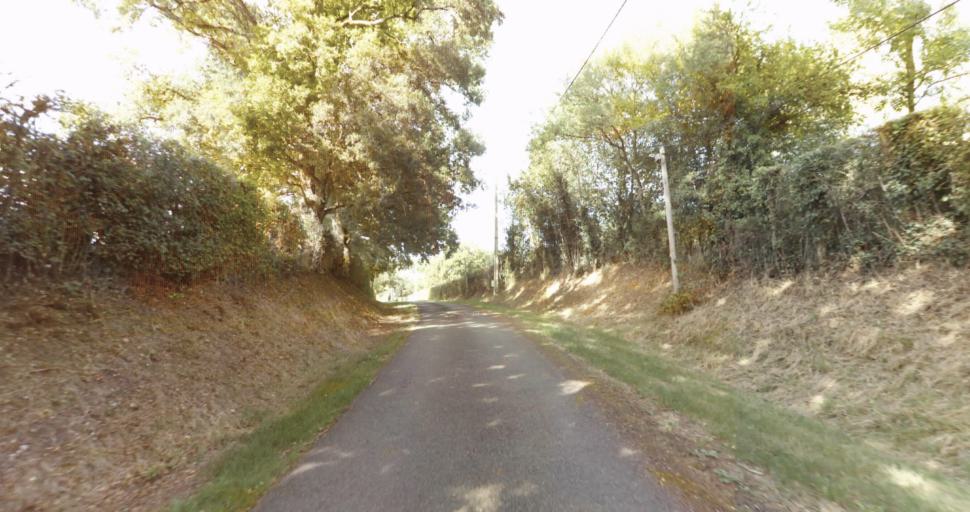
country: FR
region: Lower Normandy
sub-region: Departement de l'Orne
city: Sees
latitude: 48.7064
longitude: 0.1771
